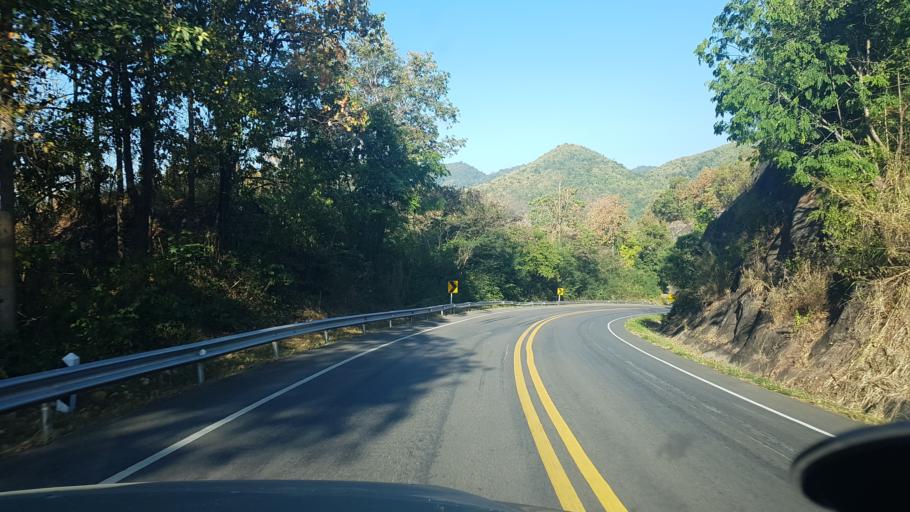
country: TH
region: Phetchabun
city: Lom Sak
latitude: 16.7425
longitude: 101.4032
